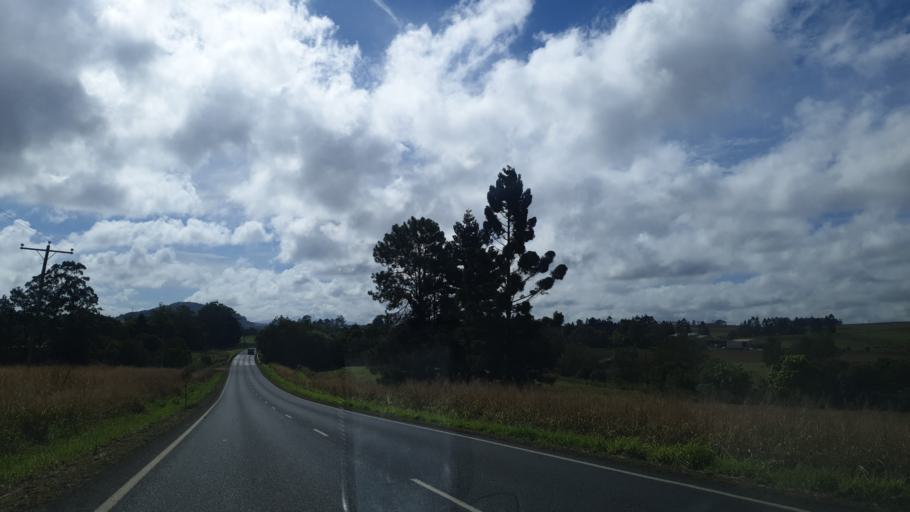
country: AU
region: Queensland
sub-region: Tablelands
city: Atherton
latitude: -17.2941
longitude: 145.5311
